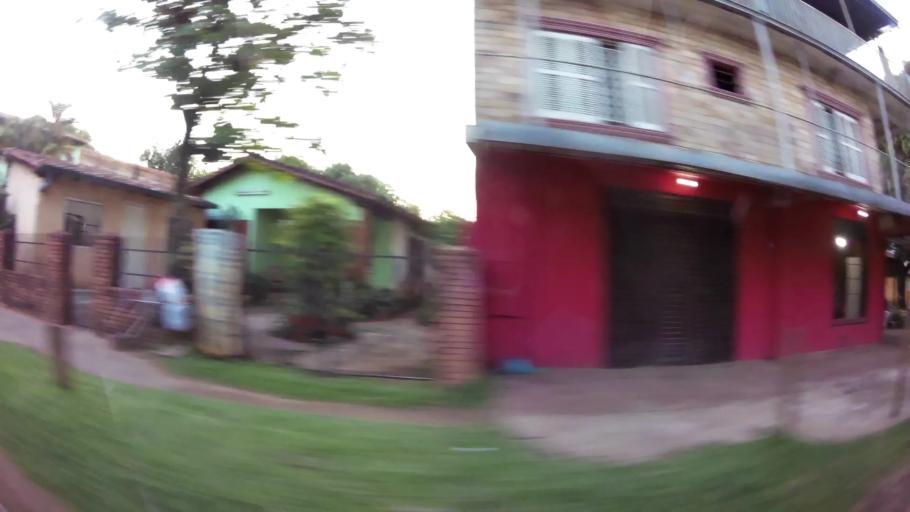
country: PY
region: Central
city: San Lorenzo
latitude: -25.3615
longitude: -57.4901
